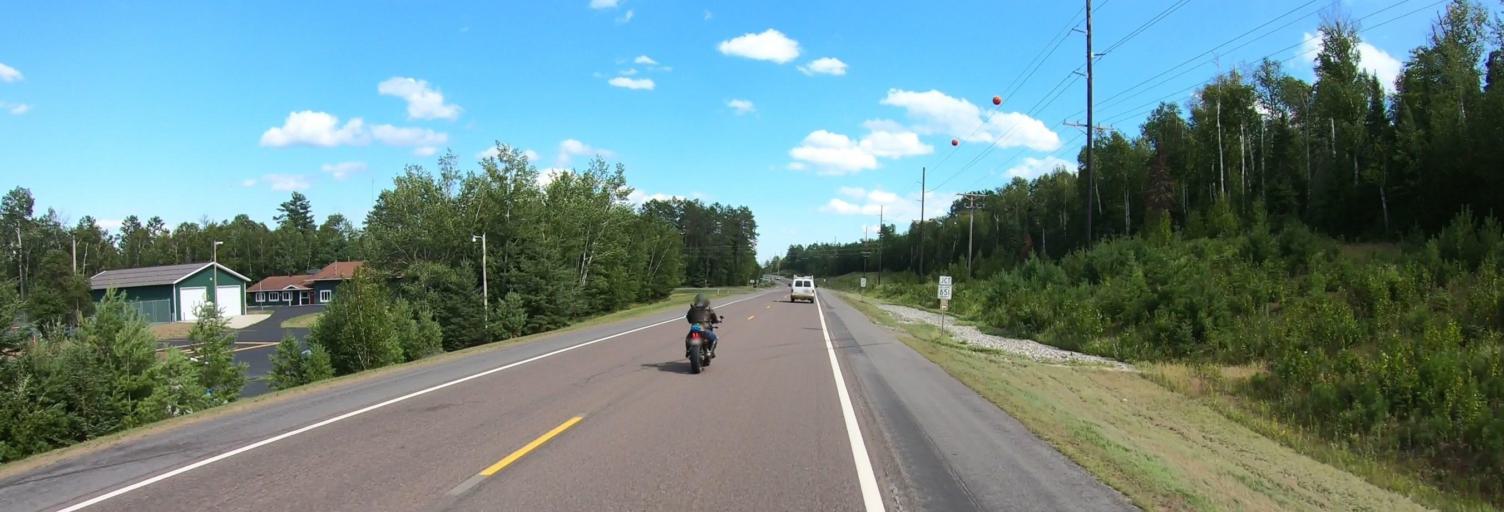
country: US
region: Minnesota
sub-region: Saint Louis County
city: Virginia
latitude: 47.8505
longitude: -92.4012
